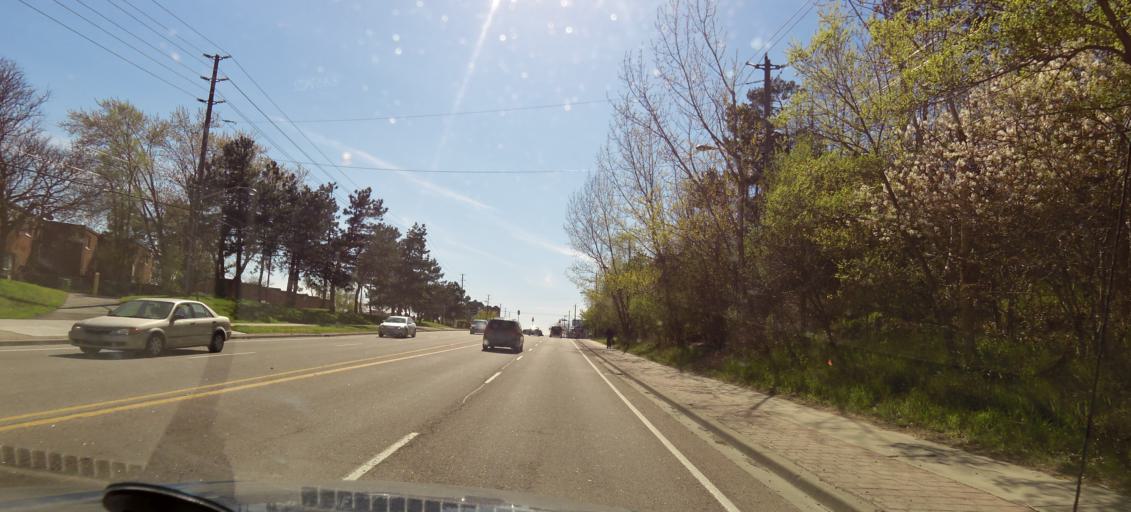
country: CA
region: Ontario
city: Concord
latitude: 43.7493
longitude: -79.5557
